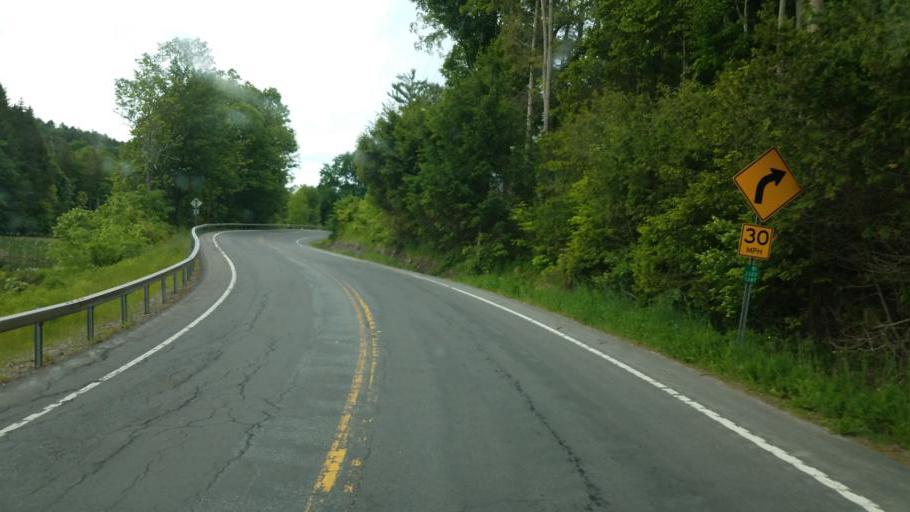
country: US
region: New York
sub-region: Herkimer County
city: Ilion
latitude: 42.9361
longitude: -75.1132
